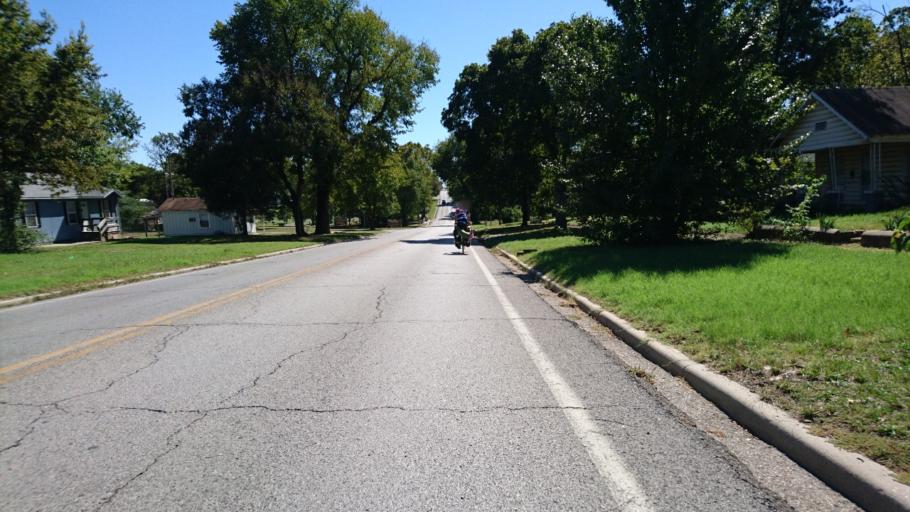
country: US
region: Kansas
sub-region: Cherokee County
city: Baxter Springs
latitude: 37.0306
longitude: -94.7348
